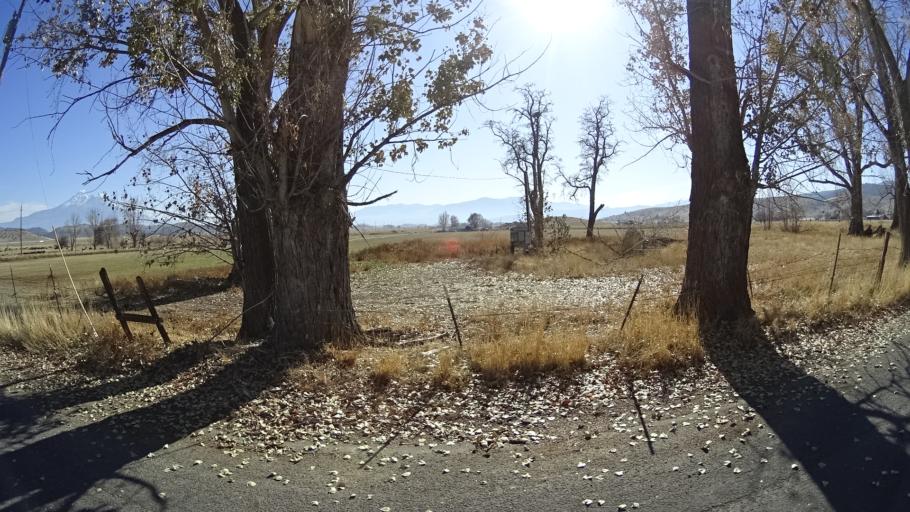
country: US
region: California
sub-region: Siskiyou County
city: Montague
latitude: 41.6181
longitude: -122.5240
